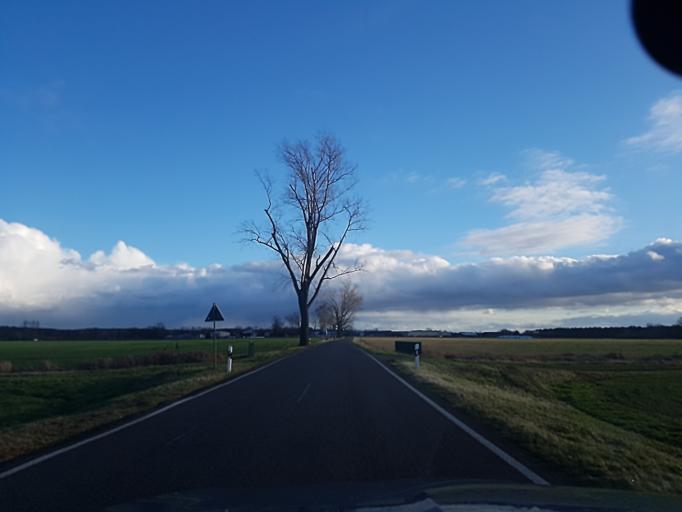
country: DE
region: Brandenburg
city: Schilda
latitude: 51.5578
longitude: 13.3506
